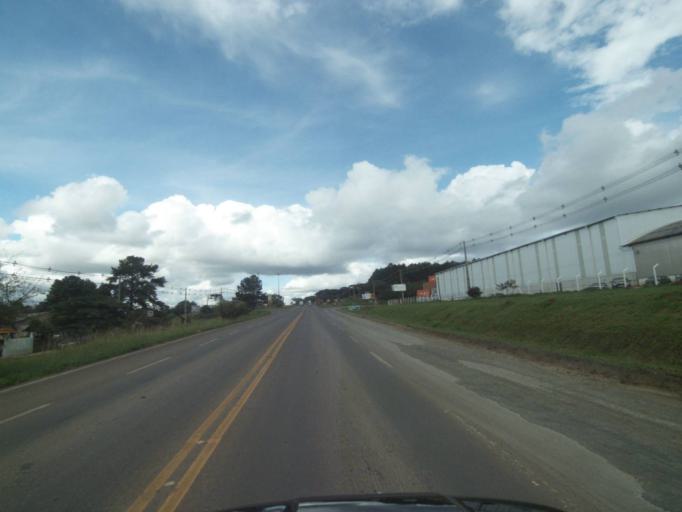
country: BR
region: Parana
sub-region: Telemaco Borba
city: Telemaco Borba
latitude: -24.3813
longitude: -50.6715
